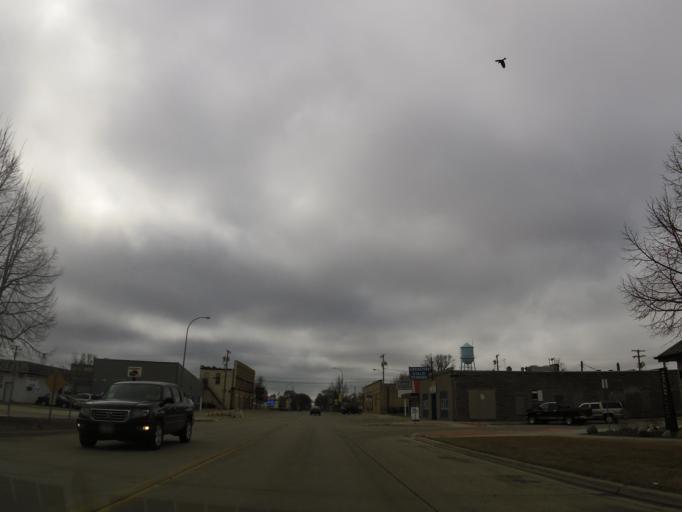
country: US
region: North Dakota
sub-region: Cass County
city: Casselton
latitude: 46.9020
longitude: -97.2112
